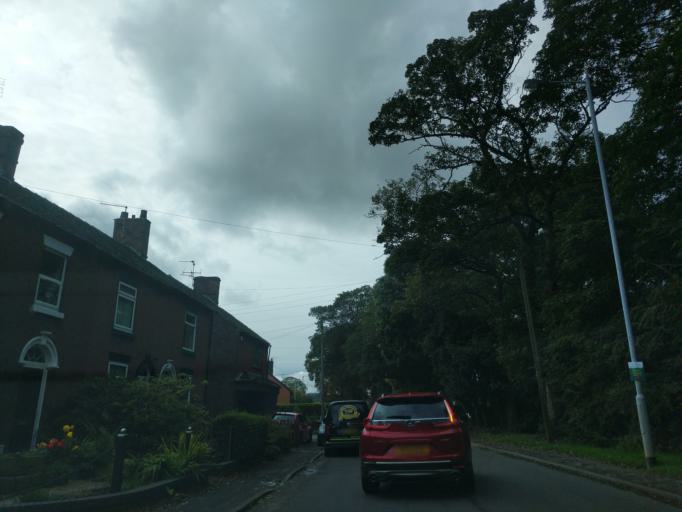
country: GB
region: England
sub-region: Staffordshire
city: Audley
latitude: 53.0038
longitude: -2.3354
